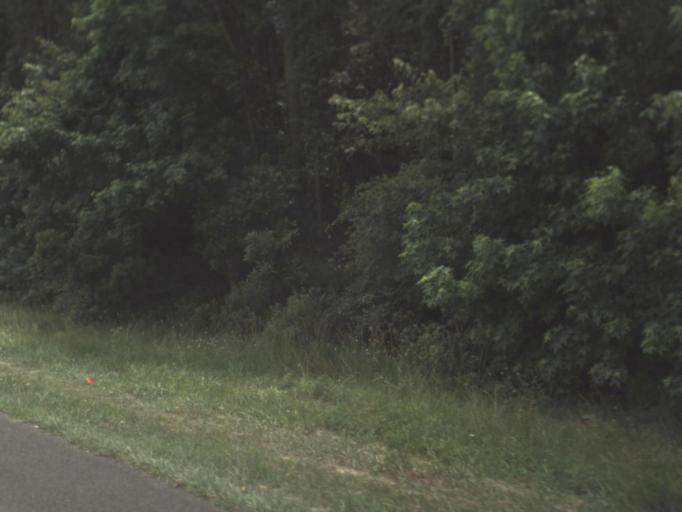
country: US
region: Florida
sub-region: Nassau County
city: Nassau Village-Ratliff
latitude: 30.4384
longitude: -81.7196
